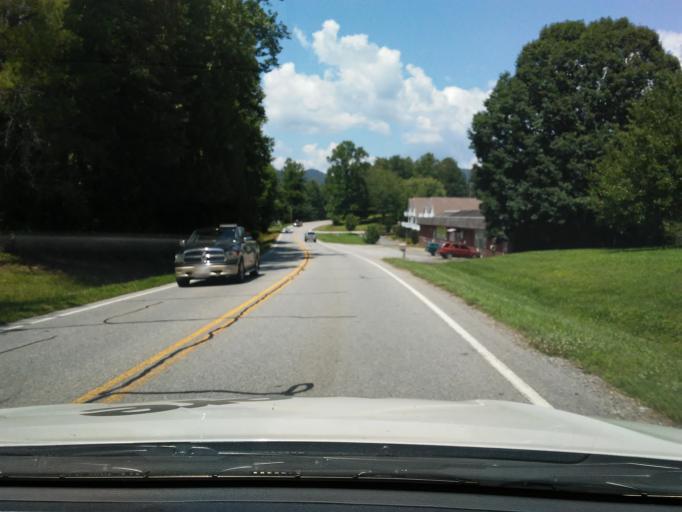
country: US
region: Georgia
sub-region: Towns County
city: Hiawassee
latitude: 34.9627
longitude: -83.7461
